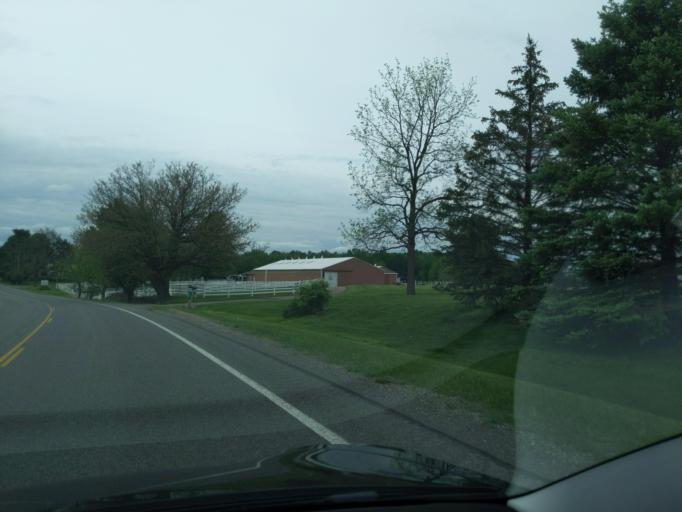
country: US
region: Michigan
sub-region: Ingham County
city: Mason
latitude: 42.5980
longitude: -84.4434
